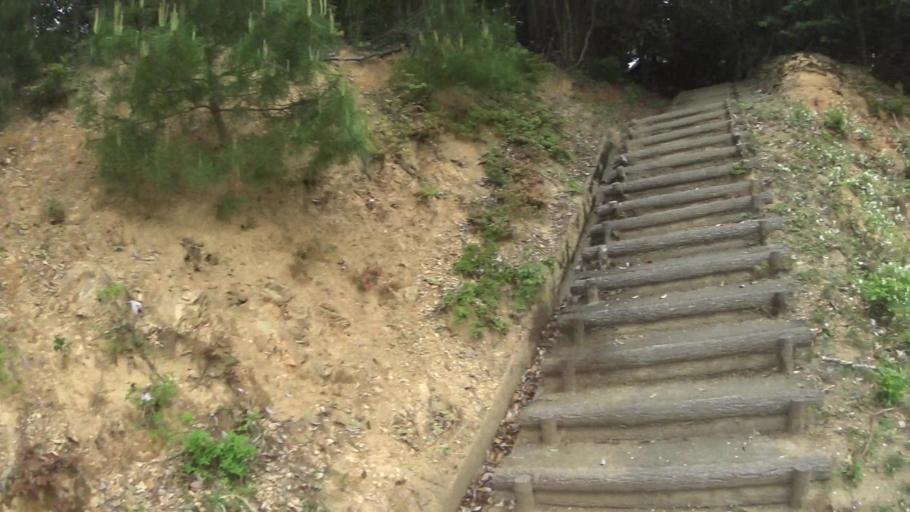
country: JP
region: Kyoto
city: Maizuru
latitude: 35.3862
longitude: 135.4413
